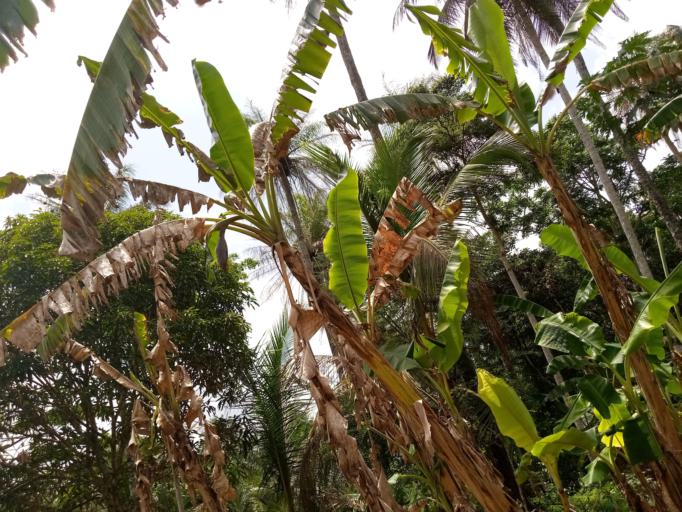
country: SL
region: Western Area
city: Waterloo
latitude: 8.4304
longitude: -13.0131
